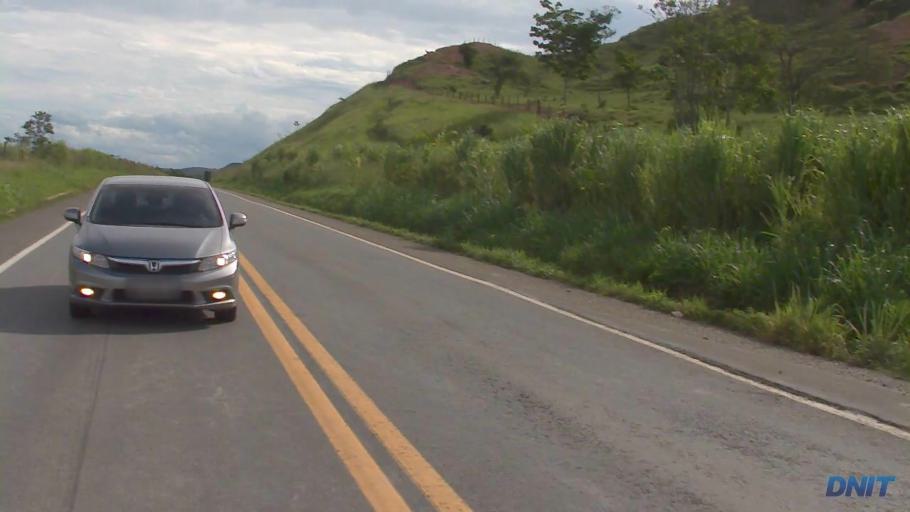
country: BR
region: Minas Gerais
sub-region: Belo Oriente
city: Belo Oriente
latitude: -19.1851
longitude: -42.2646
